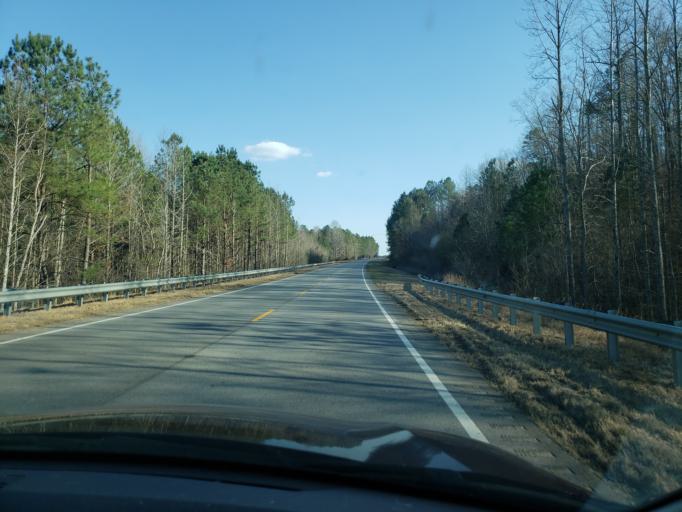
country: US
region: Alabama
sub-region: Cleburne County
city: Heflin
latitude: 33.4767
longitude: -85.5847
